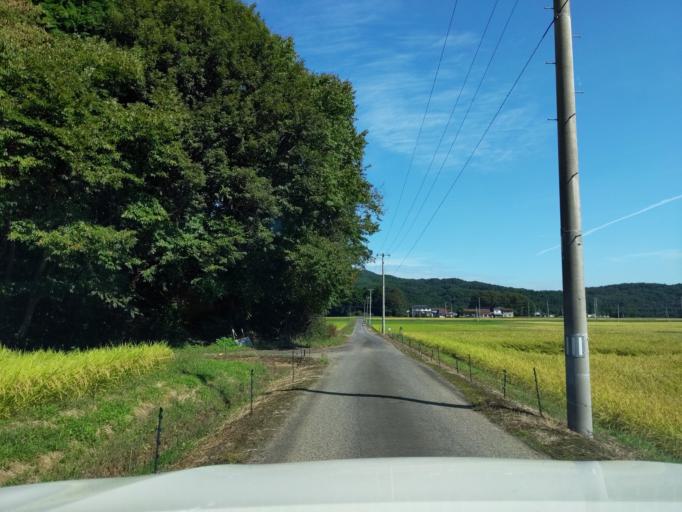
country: JP
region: Fukushima
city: Koriyama
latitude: 37.4056
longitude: 140.2395
